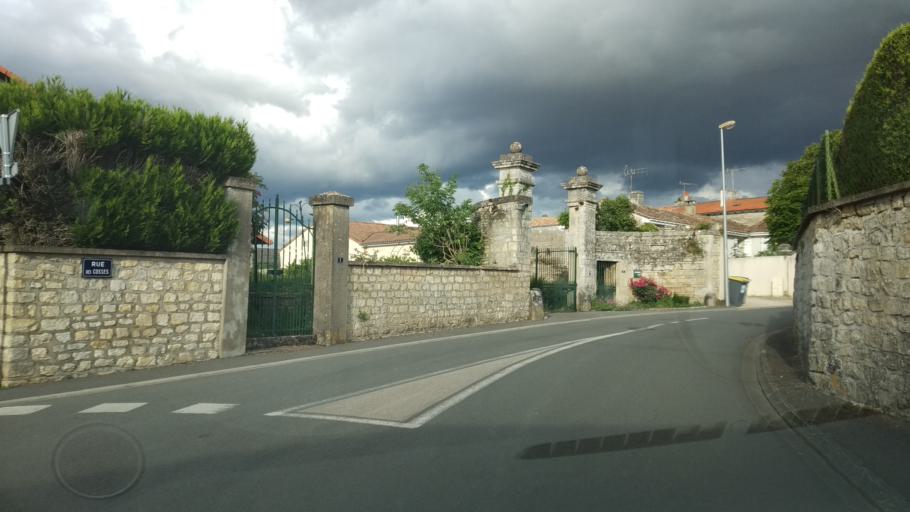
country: FR
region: Poitou-Charentes
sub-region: Departement de la Vienne
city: Migne-Auxances
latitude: 46.6290
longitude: 0.3348
